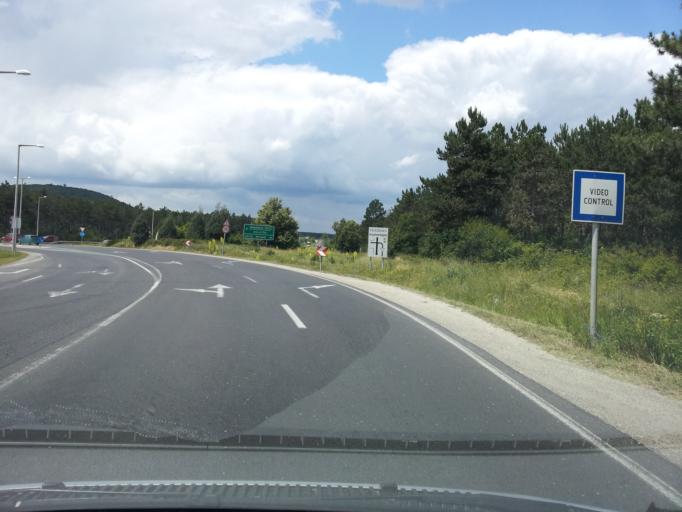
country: HU
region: Veszprem
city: Veszprem
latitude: 47.1081
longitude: 17.8674
